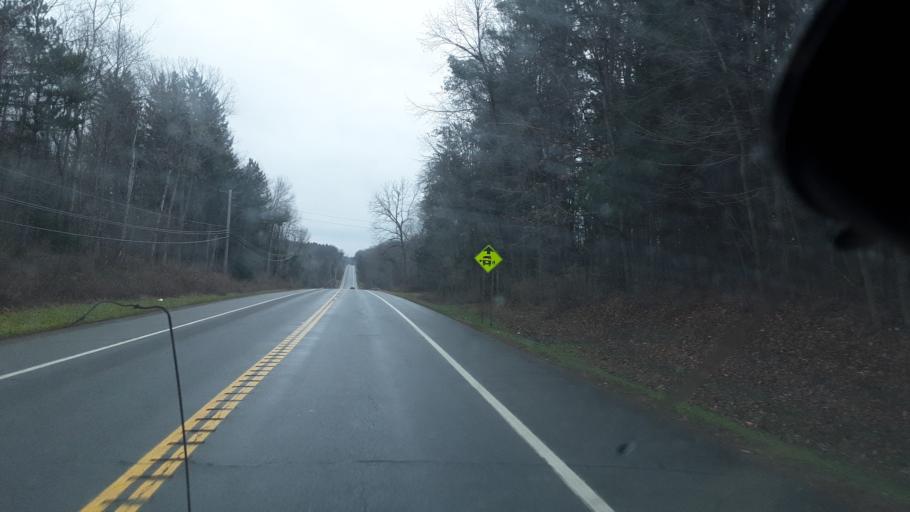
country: US
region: New York
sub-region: Erie County
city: Holland
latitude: 42.6134
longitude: -78.5082
